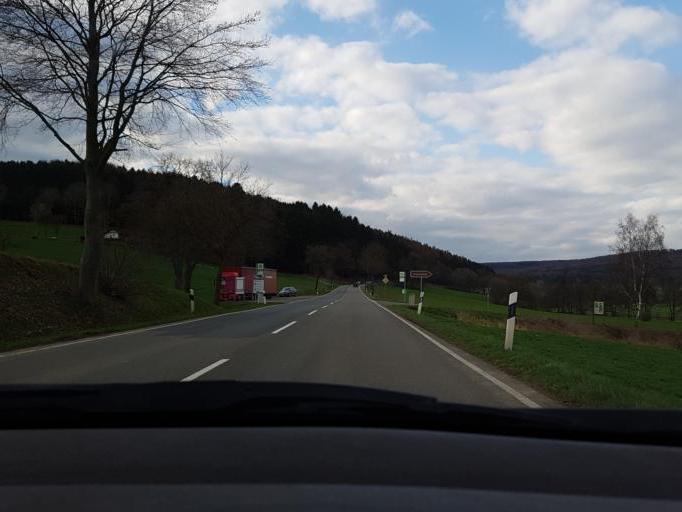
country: DE
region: Lower Saxony
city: Bodenfelde
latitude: 51.6969
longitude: 9.5520
